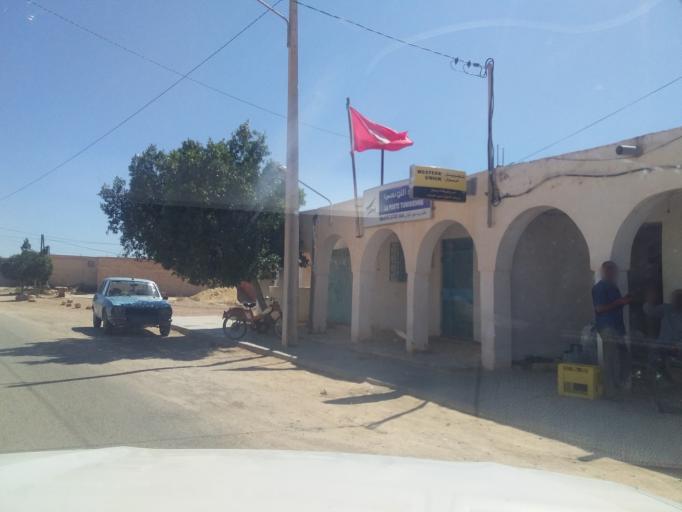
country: TN
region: Qabis
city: Matmata
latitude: 33.5140
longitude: 10.2179
